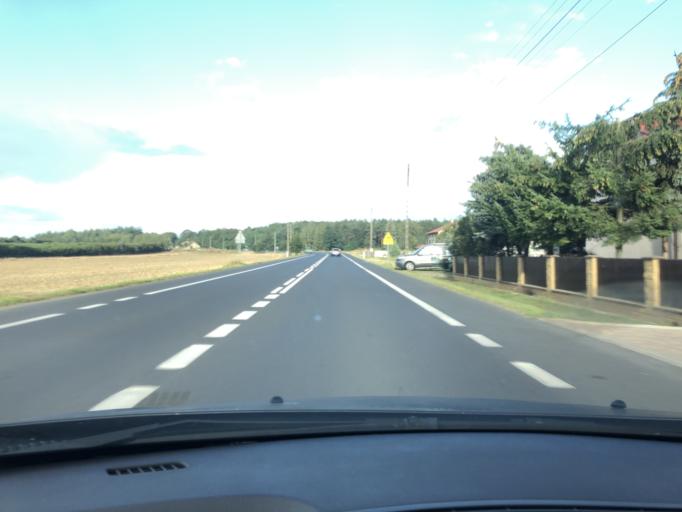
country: PL
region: Lodz Voivodeship
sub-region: Powiat wieruszowski
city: Galewice
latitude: 51.3043
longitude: 18.2366
